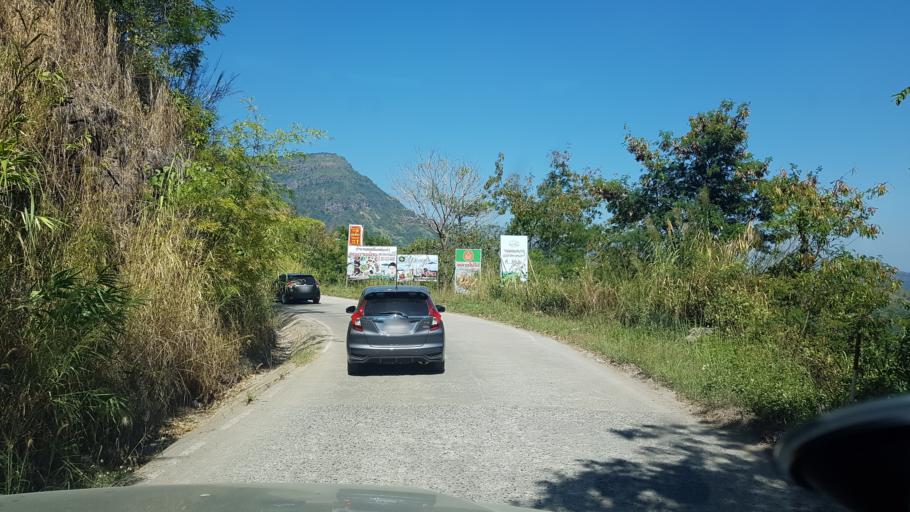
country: TH
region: Phetchabun
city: Khao Kho
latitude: 16.7849
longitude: 101.0515
